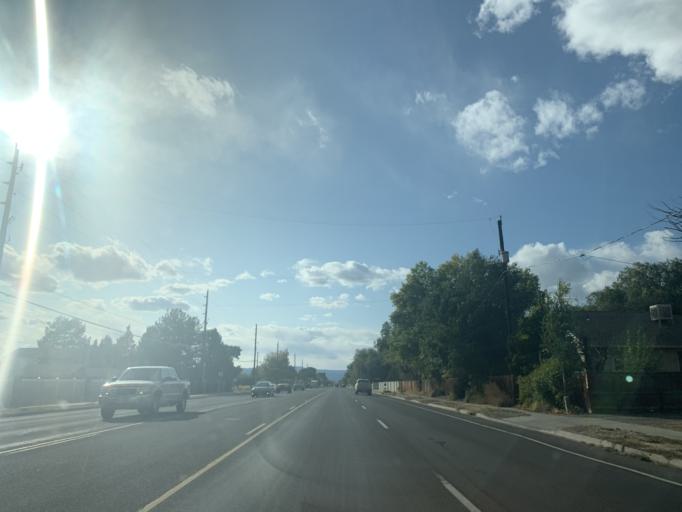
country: US
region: Colorado
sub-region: Mesa County
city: Fruitvale
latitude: 39.0918
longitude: -108.4804
